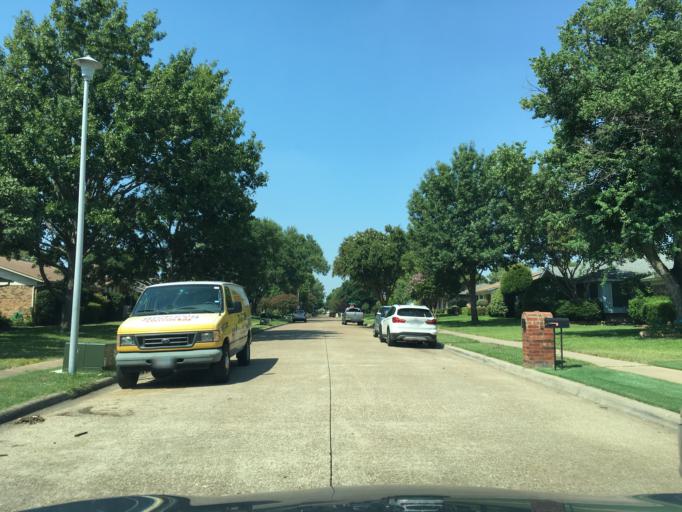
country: US
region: Texas
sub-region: Dallas County
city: Garland
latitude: 32.9365
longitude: -96.6512
